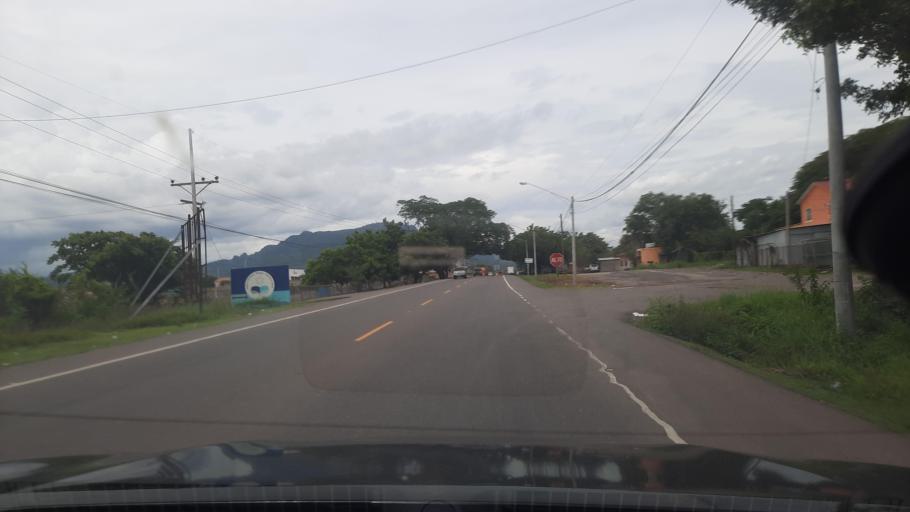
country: HN
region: Valle
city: Jicaro Galan
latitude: 13.5320
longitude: -87.4451
